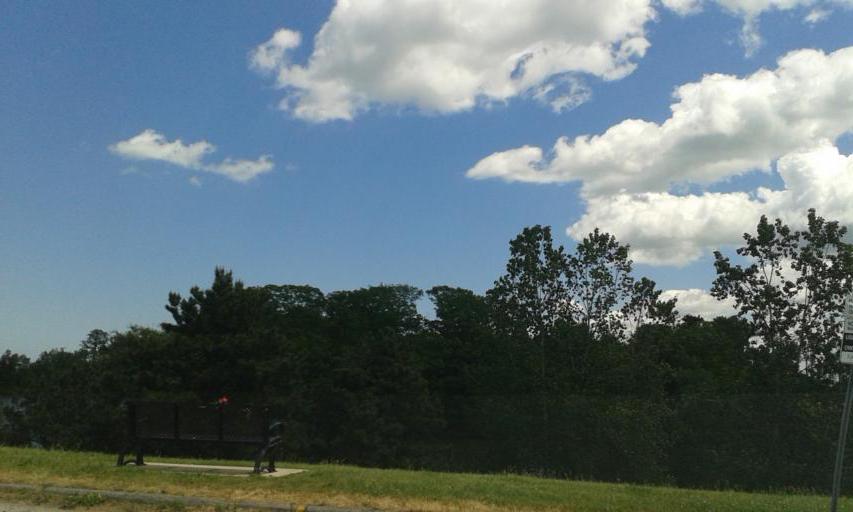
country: CA
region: Ontario
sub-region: Regional Municipality of Niagara
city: St. Catharines
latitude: 43.1808
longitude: -79.3224
